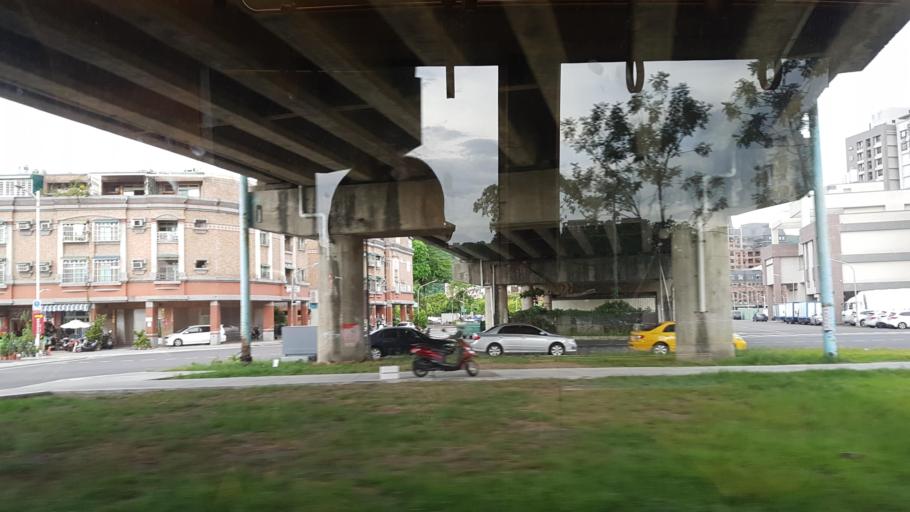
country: TW
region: Kaohsiung
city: Kaohsiung
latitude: 22.6455
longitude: 120.2812
